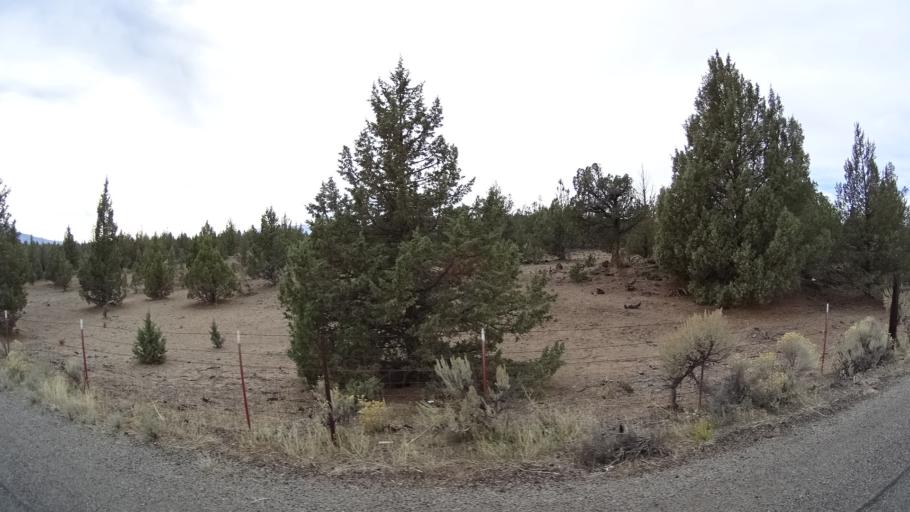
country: US
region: California
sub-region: Siskiyou County
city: Weed
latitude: 41.6071
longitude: -122.3623
